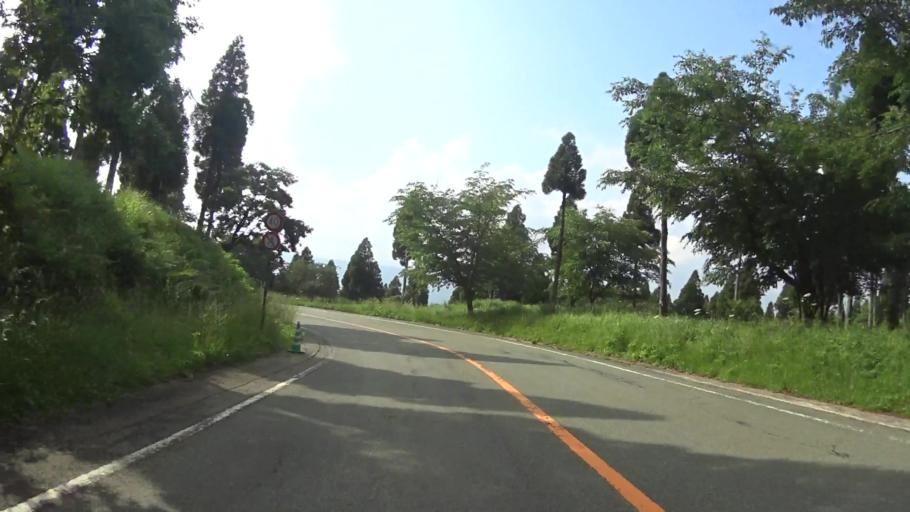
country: JP
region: Kumamoto
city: Aso
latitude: 32.8929
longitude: 131.0490
